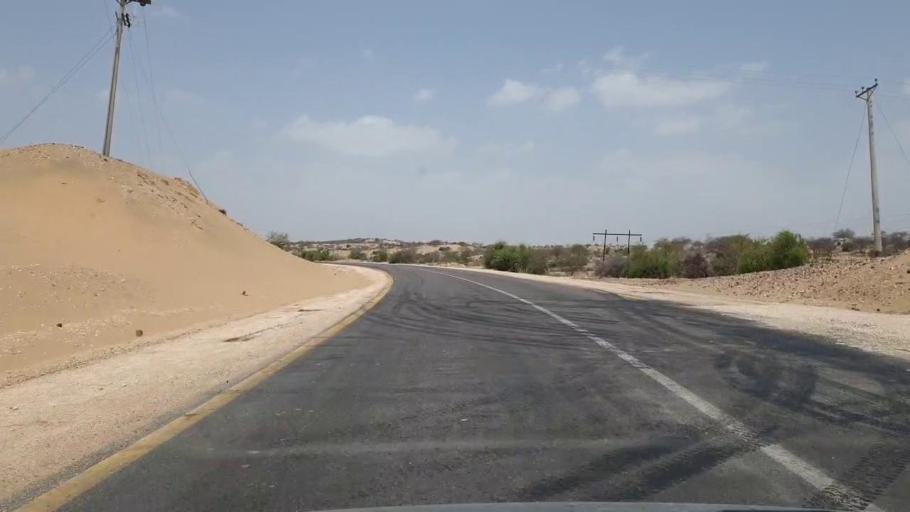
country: PK
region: Sindh
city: Mithi
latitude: 24.8399
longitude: 69.6675
